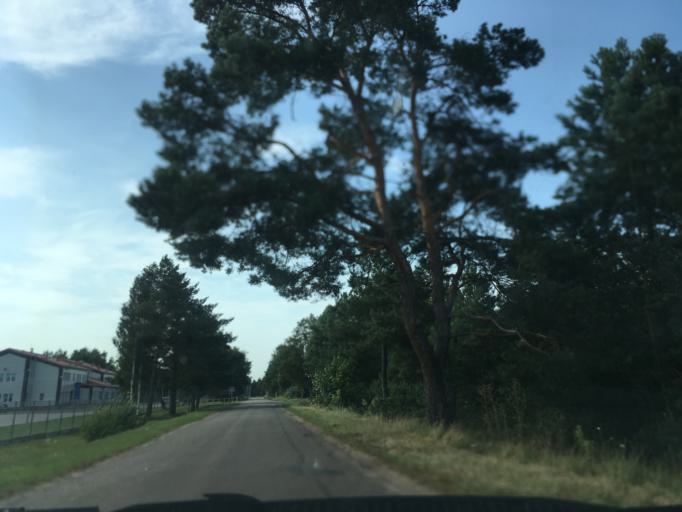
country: PL
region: Podlasie
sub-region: Powiat hajnowski
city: Bialowieza
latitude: 52.9021
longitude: 23.8297
